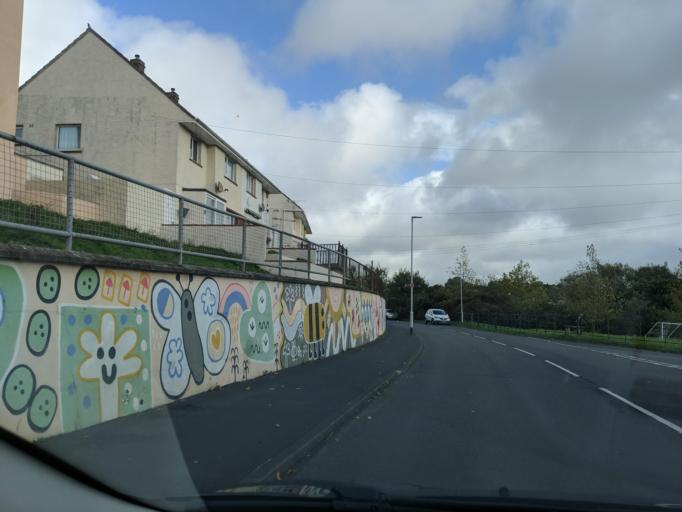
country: GB
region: England
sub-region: Cornwall
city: Torpoint
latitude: 50.3985
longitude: -4.1863
